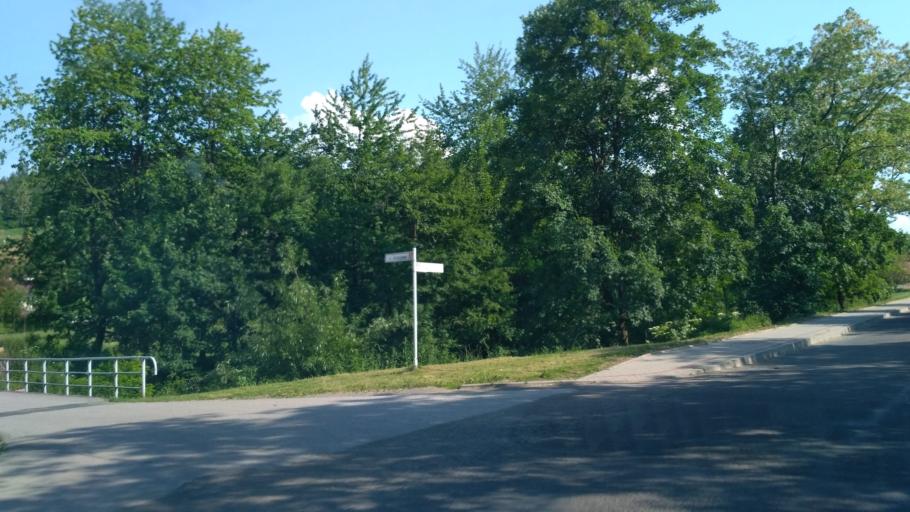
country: PL
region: Subcarpathian Voivodeship
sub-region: Powiat jaroslawski
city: Pruchnik
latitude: 49.8898
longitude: 22.4979
